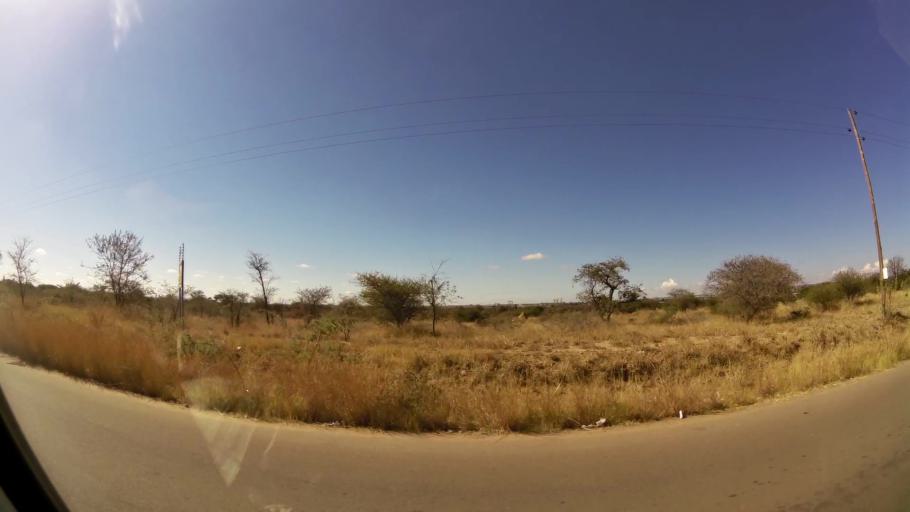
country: ZA
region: Limpopo
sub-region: Capricorn District Municipality
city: Polokwane
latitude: -23.8632
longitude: 29.4276
